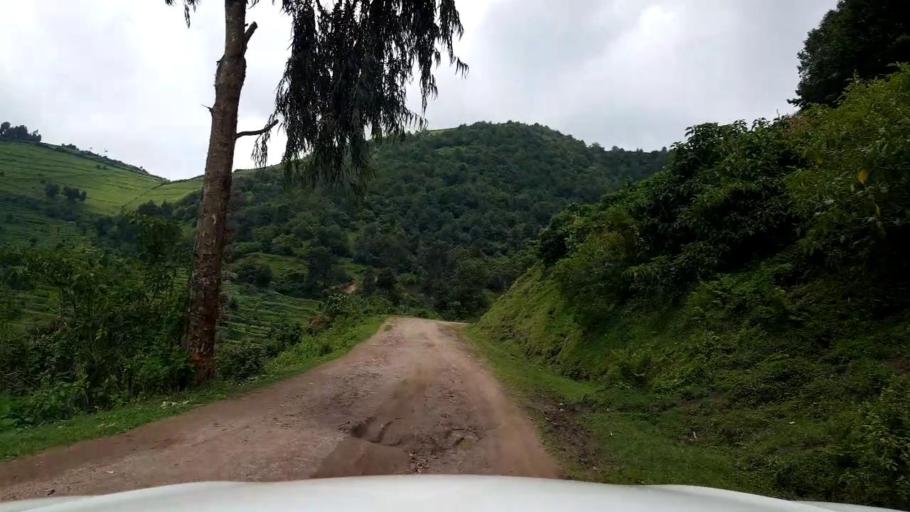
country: RW
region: Western Province
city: Gisenyi
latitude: -1.6667
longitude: 29.4160
